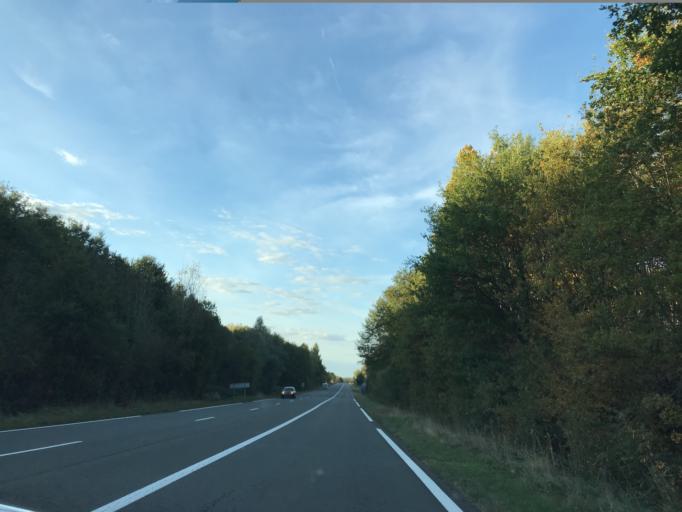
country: FR
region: Auvergne
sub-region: Departement de l'Allier
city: Saint-Yorre
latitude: 46.0135
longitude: 3.4854
